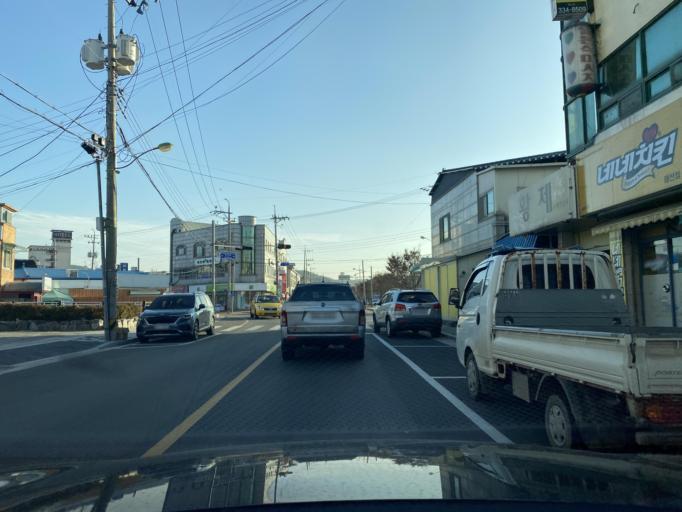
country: KR
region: Chungcheongnam-do
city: Yesan
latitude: 36.6894
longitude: 126.8298
